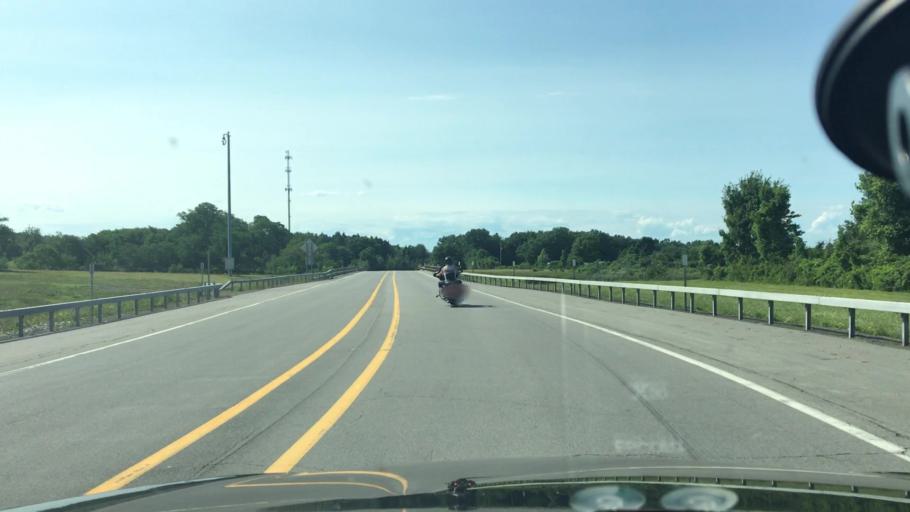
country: US
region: New York
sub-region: Chautauqua County
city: Silver Creek
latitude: 42.5505
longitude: -79.1066
